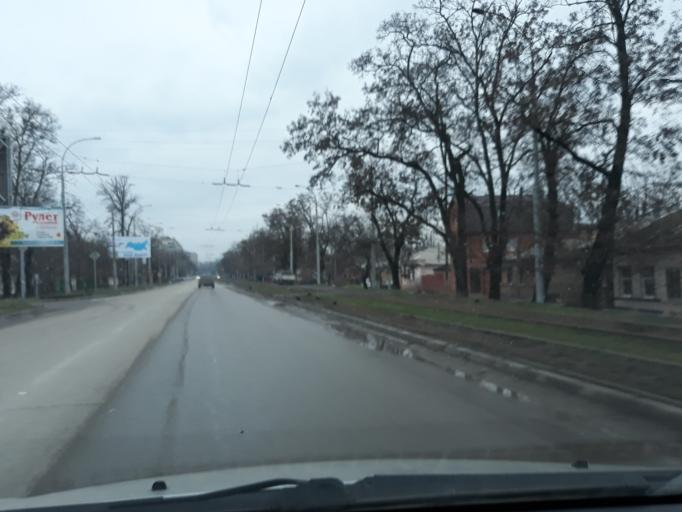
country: RU
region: Rostov
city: Taganrog
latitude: 47.2238
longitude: 38.9161
